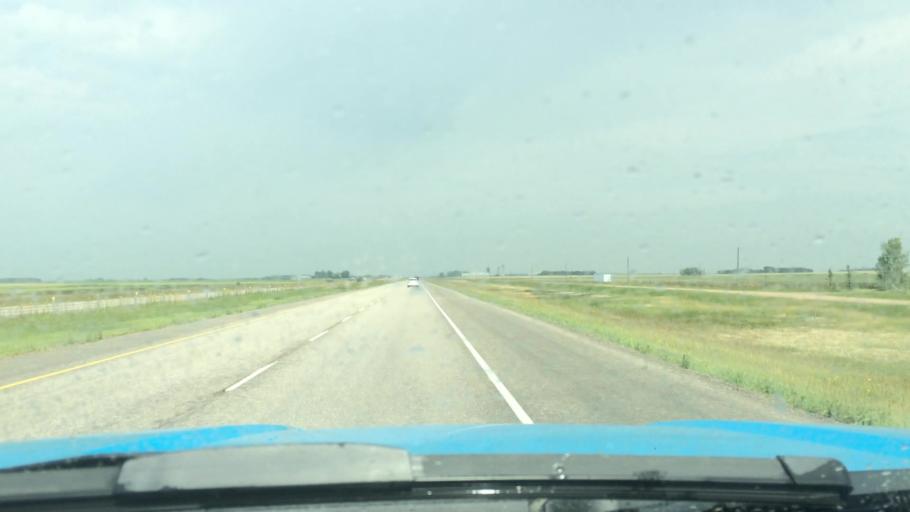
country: CA
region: Alberta
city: Olds
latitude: 51.7000
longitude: -114.0253
